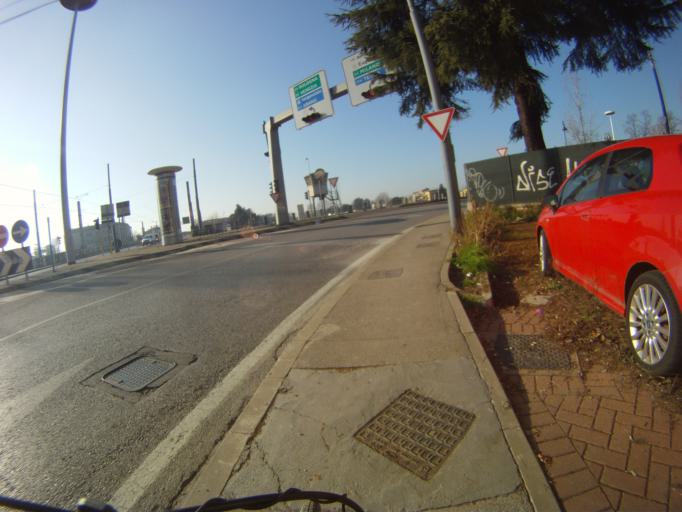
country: IT
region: Veneto
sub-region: Provincia di Padova
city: Mandriola-Sant'Agostino
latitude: 45.3871
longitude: 11.8672
